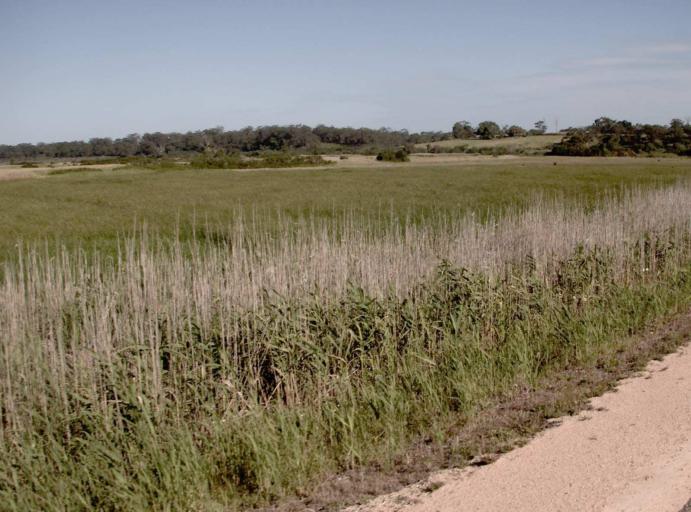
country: AU
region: Victoria
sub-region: East Gippsland
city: Lakes Entrance
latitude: -37.7748
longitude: 148.5380
